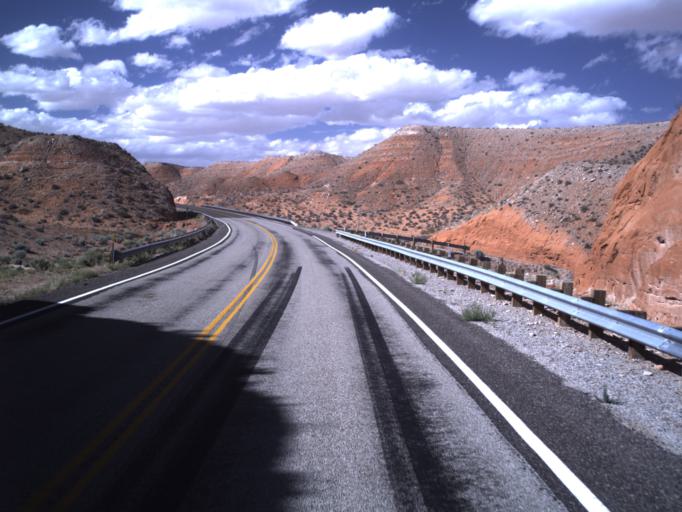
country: US
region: Utah
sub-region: Wayne County
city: Loa
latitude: 38.1409
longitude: -110.6099
